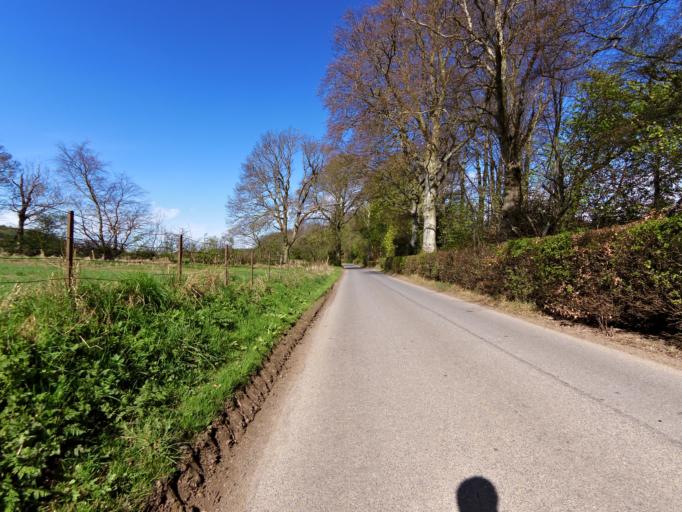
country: GB
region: Scotland
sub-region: Dundee City
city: Dundee
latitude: 56.4074
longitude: -3.0142
